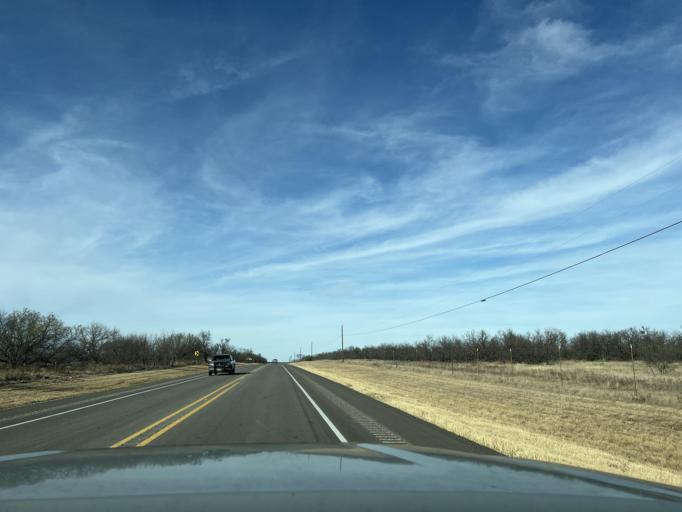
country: US
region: Texas
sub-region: Shackelford County
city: Albany
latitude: 32.6310
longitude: -99.2259
